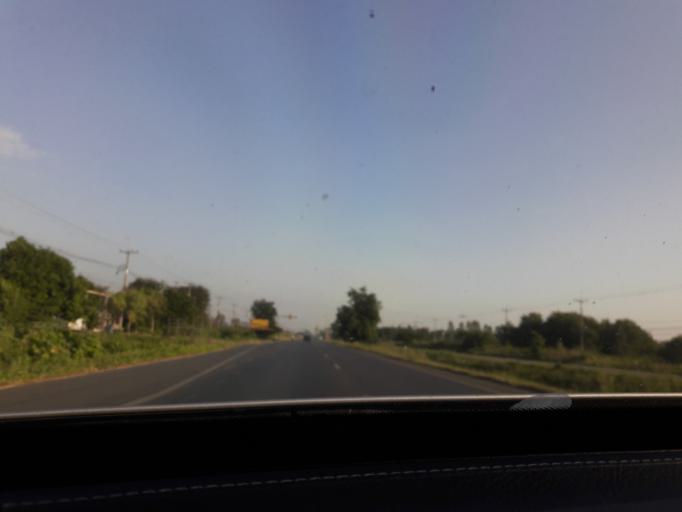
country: TH
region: Phra Nakhon Si Ayutthaya
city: Bang Pahan
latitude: 14.4322
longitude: 100.5348
